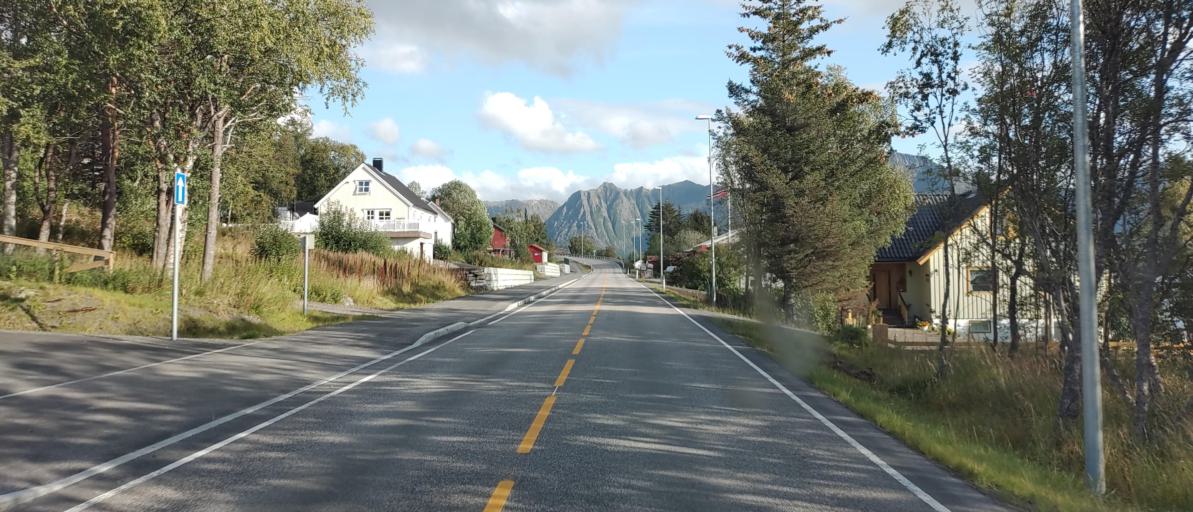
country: NO
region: Nordland
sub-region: Sortland
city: Sortland
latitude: 68.7531
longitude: 15.4711
